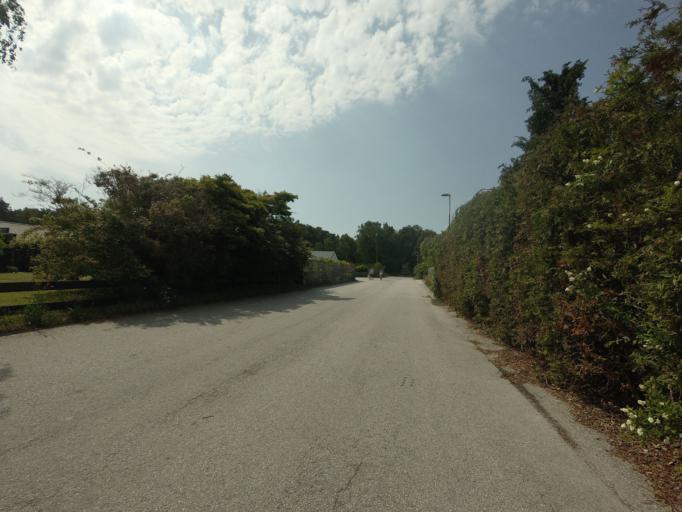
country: SE
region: Skane
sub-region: Vellinge Kommun
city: Skanor med Falsterbo
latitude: 55.4035
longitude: 12.8505
